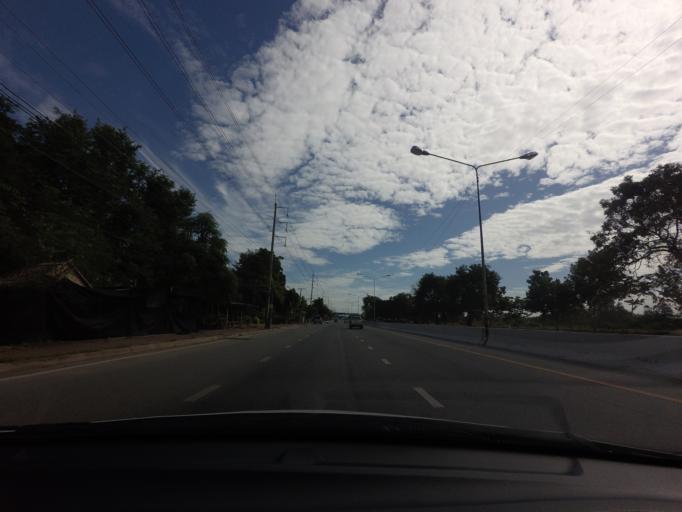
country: TH
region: Pathum Thani
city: Nong Suea
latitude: 14.0831
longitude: 100.9107
